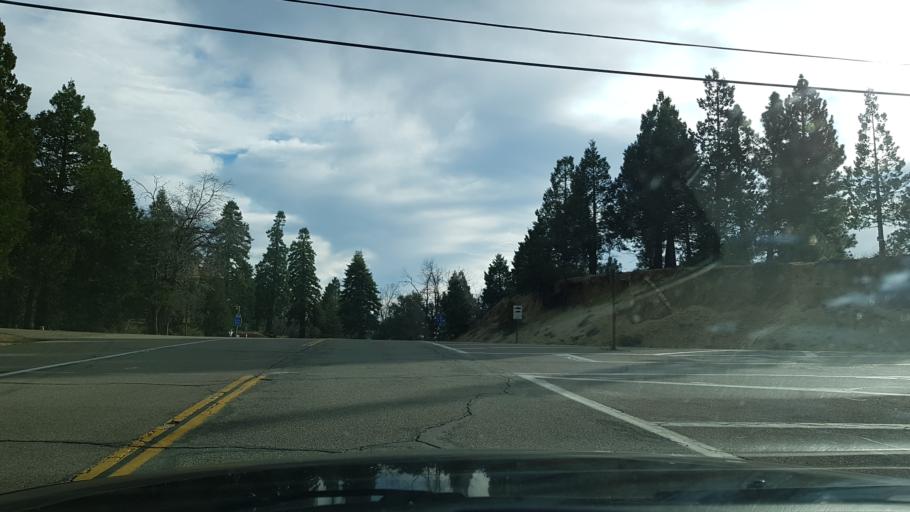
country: US
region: California
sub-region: Riverside County
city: Aguanga
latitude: 33.3142
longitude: -116.8652
